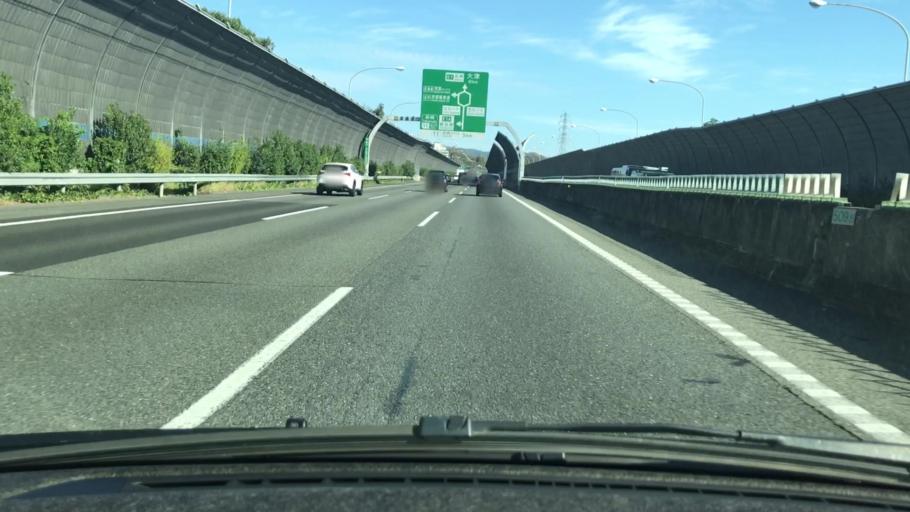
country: JP
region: Osaka
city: Ibaraki
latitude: 34.8444
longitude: 135.5745
